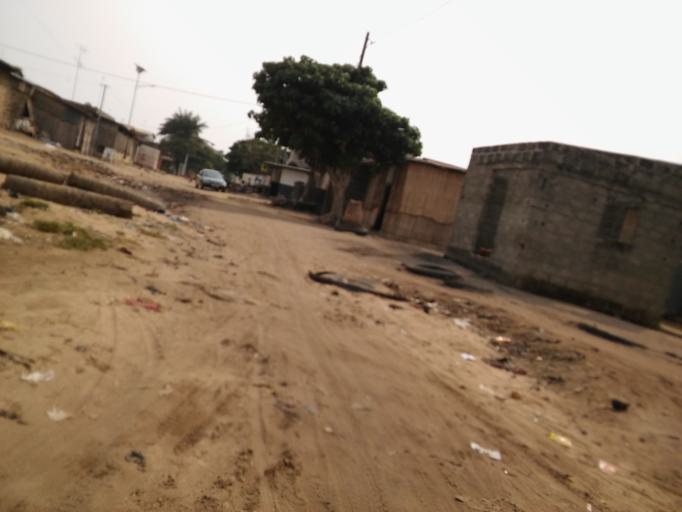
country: BJ
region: Littoral
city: Cotonou
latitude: 6.3934
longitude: 2.3763
